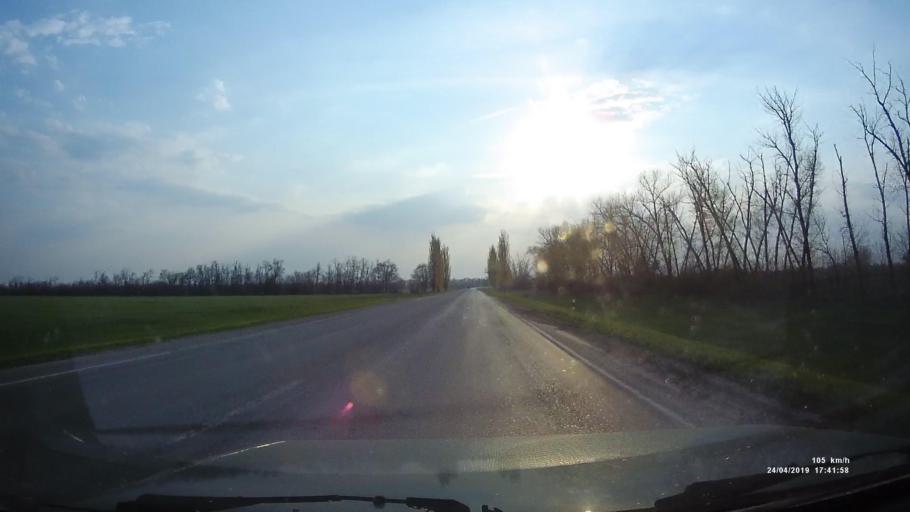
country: RU
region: Rostov
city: Tselina
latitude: 46.5316
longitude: 40.9580
